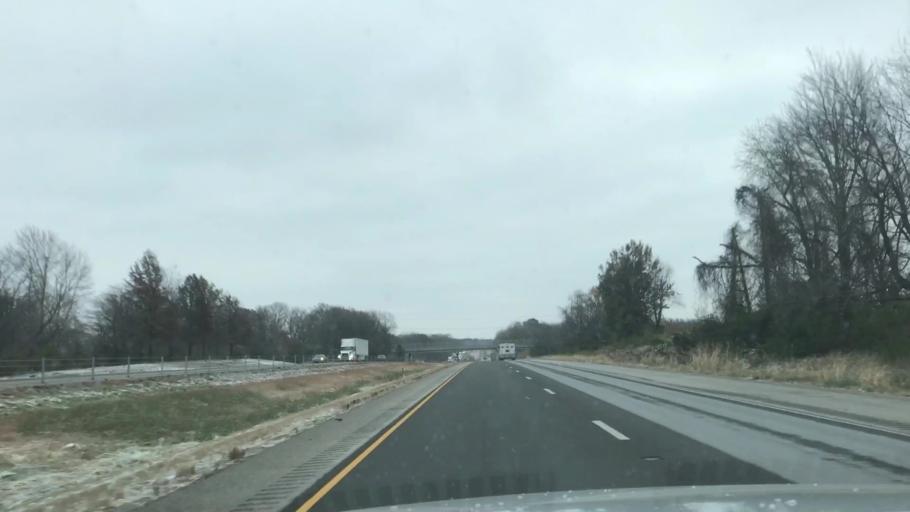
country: US
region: Illinois
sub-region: Madison County
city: Glen Carbon
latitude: 38.7566
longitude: -89.9885
